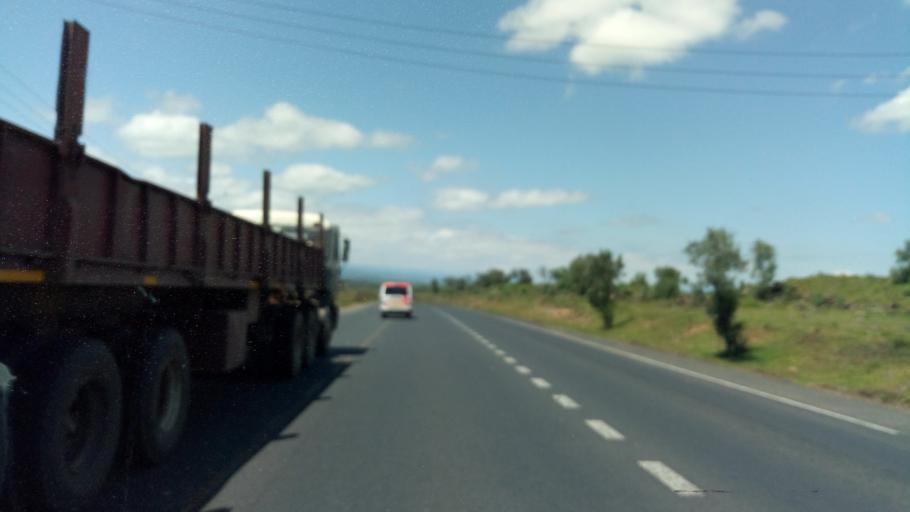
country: KE
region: Nakuru
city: Naivasha
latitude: -0.5403
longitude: 36.3372
